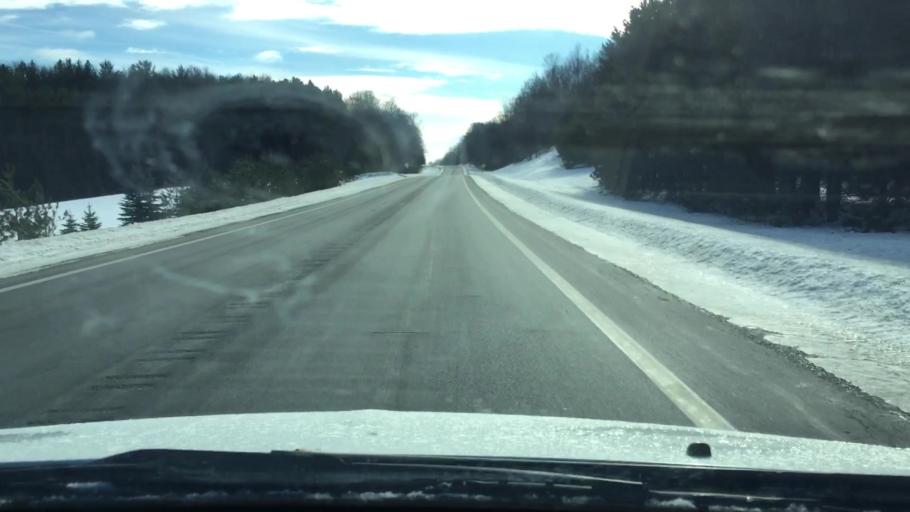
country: US
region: Michigan
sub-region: Antrim County
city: Mancelona
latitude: 44.9792
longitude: -85.0539
